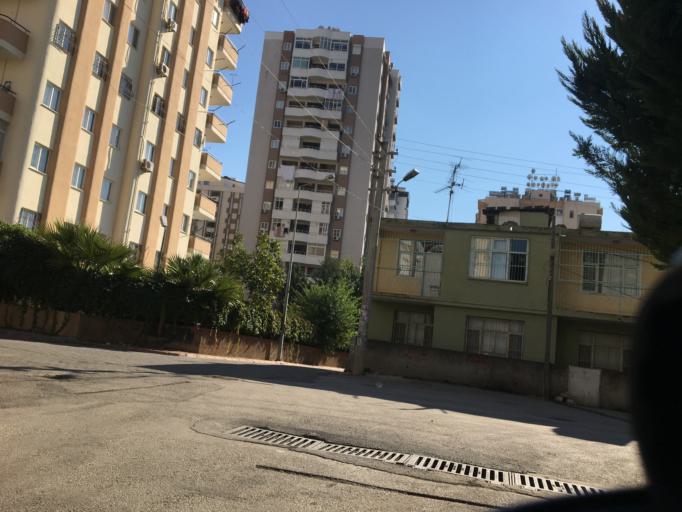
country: TR
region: Adana
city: Seyhan
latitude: 37.0258
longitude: 35.2856
